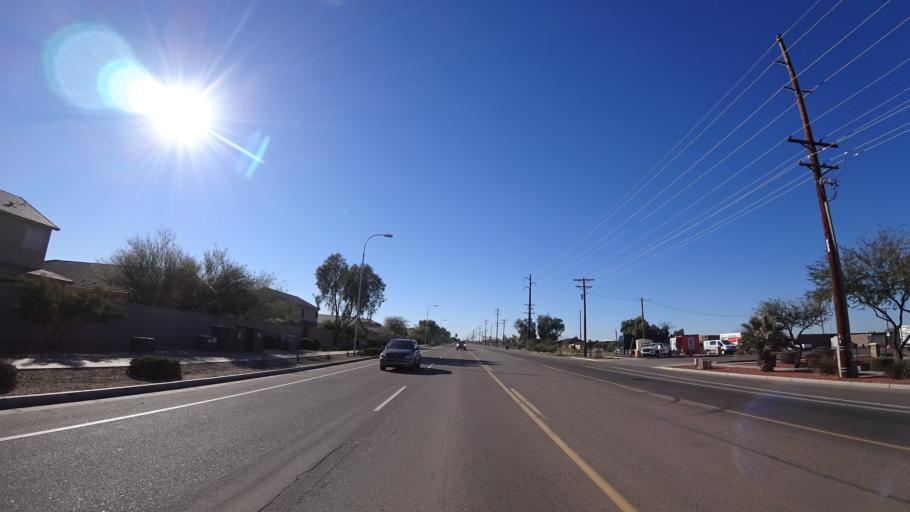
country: US
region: Arizona
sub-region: Maricopa County
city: Laveen
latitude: 33.3920
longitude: -112.1537
